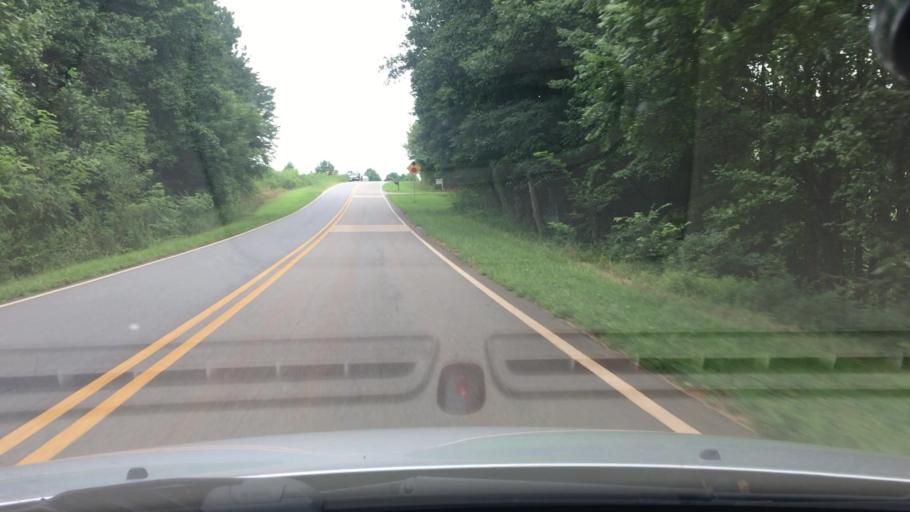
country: US
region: Georgia
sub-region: Lumpkin County
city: Dahlonega
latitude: 34.6059
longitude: -83.8973
